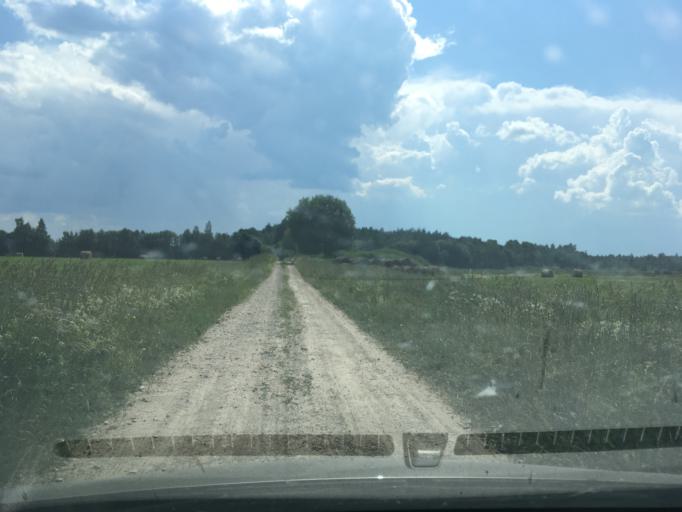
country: EE
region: Raplamaa
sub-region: Maerjamaa vald
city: Marjamaa
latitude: 58.8036
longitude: 24.4598
